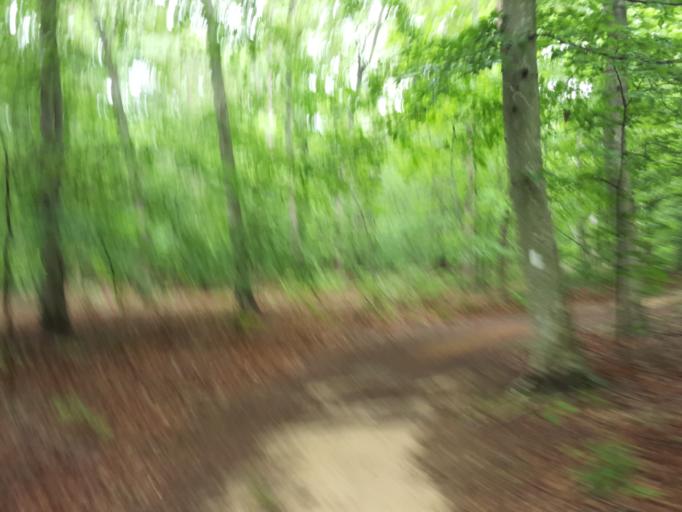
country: US
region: Maryland
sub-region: Prince George's County
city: Marlboro Meadows
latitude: 38.8027
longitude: -76.6956
